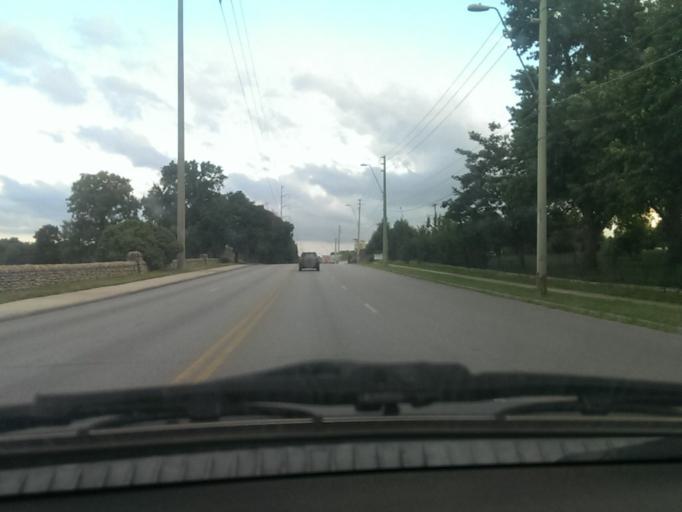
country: US
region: Kansas
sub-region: Johnson County
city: Mission Hills
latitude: 39.0017
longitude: -94.5752
